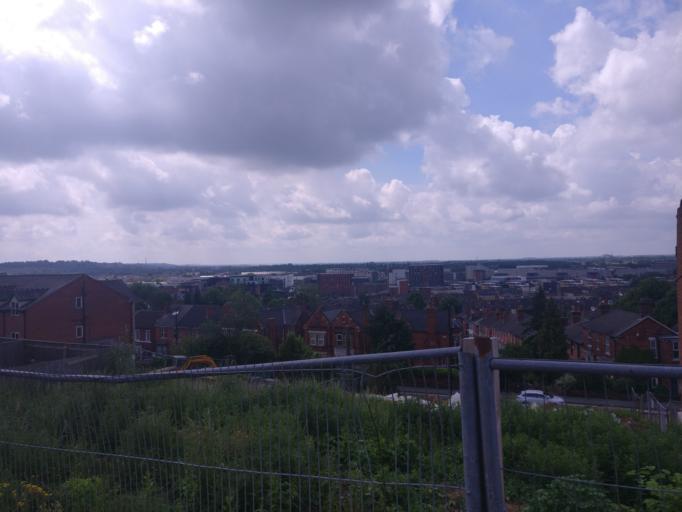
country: GB
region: England
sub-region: Lincolnshire
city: Lincoln
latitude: 53.2343
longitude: -0.5462
